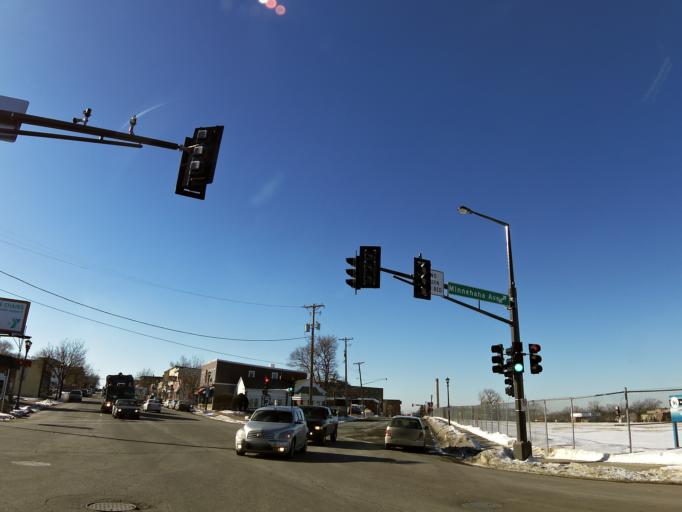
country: US
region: Minnesota
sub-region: Ramsey County
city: Saint Paul
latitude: 44.9631
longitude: -93.0634
